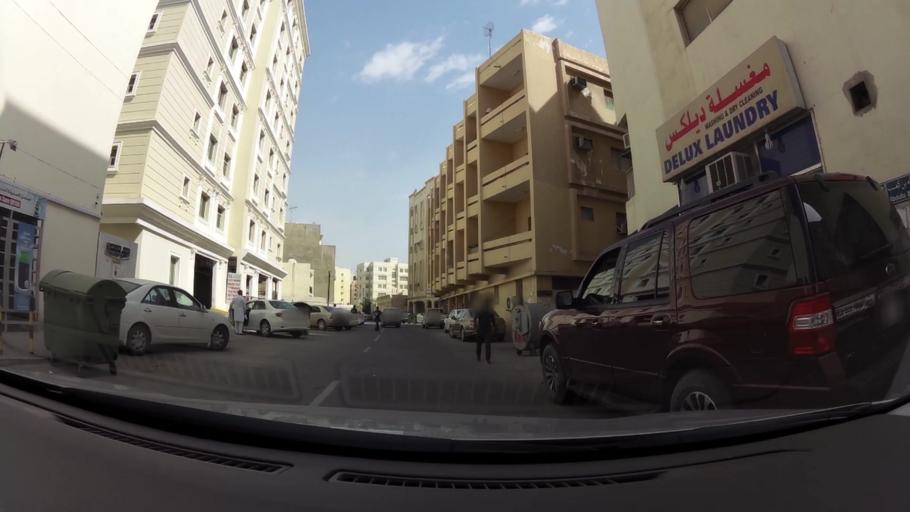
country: QA
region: Baladiyat ad Dawhah
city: Doha
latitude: 25.2841
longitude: 51.5130
